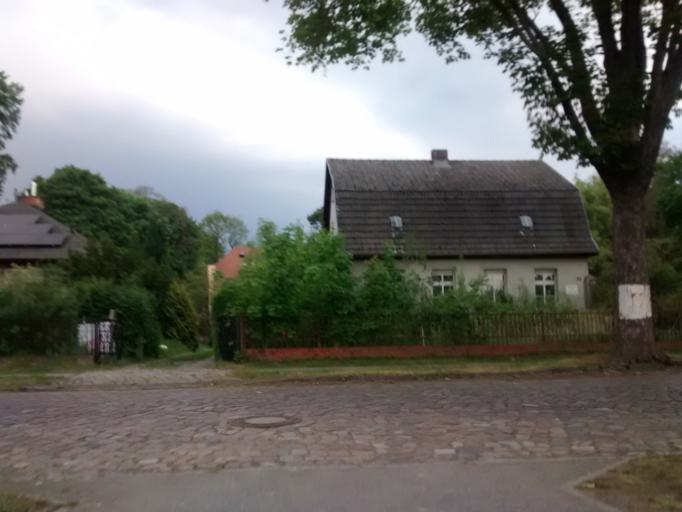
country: DE
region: Brandenburg
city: Hohen Neuendorf
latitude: 52.6654
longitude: 13.2761
